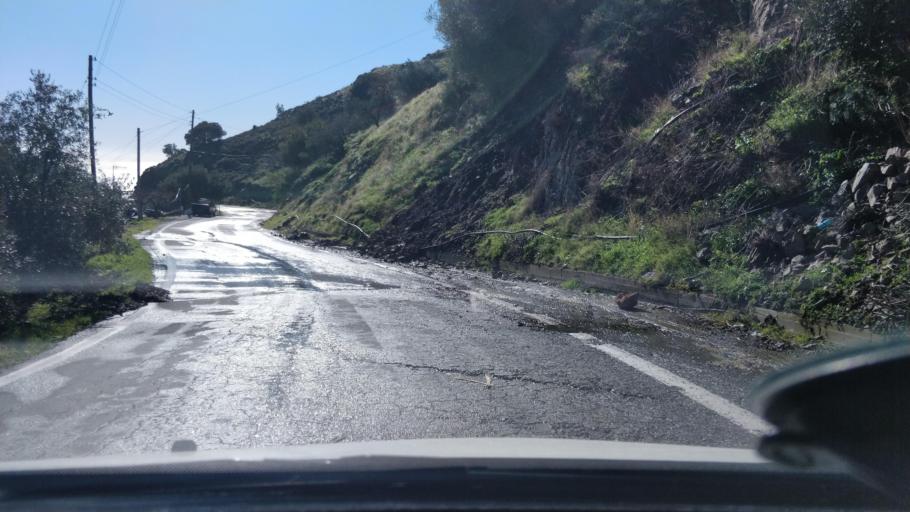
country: GR
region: Crete
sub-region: Nomos Irakleiou
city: Kastelli
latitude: 35.0394
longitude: 25.4443
